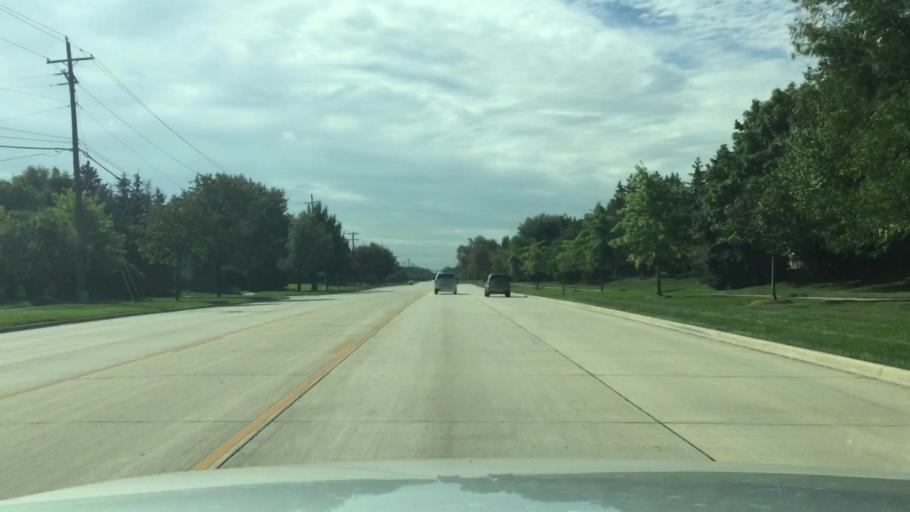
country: US
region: Michigan
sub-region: Wayne County
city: Canton
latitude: 42.3050
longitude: -83.4871
